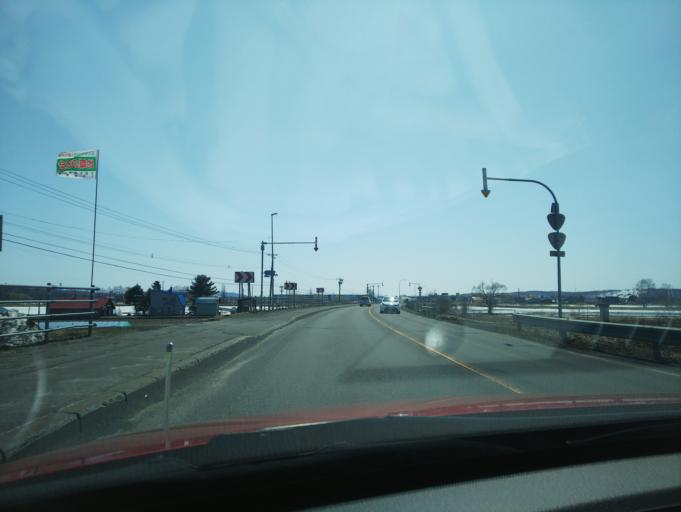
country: JP
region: Hokkaido
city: Nayoro
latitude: 44.1944
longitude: 142.3949
